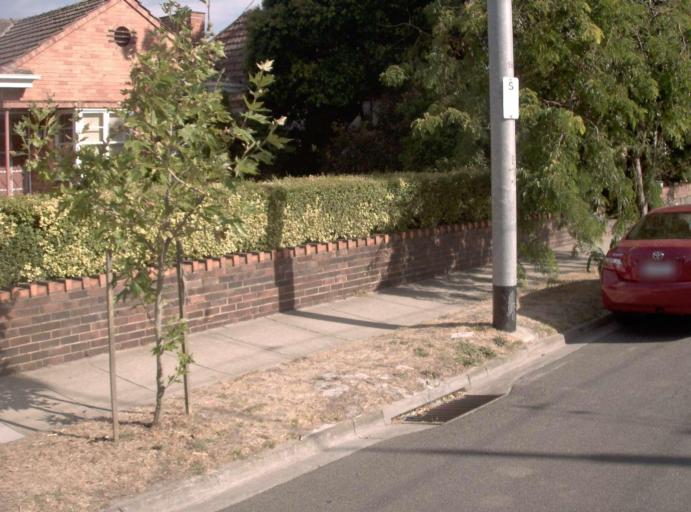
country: AU
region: Victoria
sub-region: Glen Eira
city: Caulfield South
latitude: -37.8945
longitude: 145.0205
